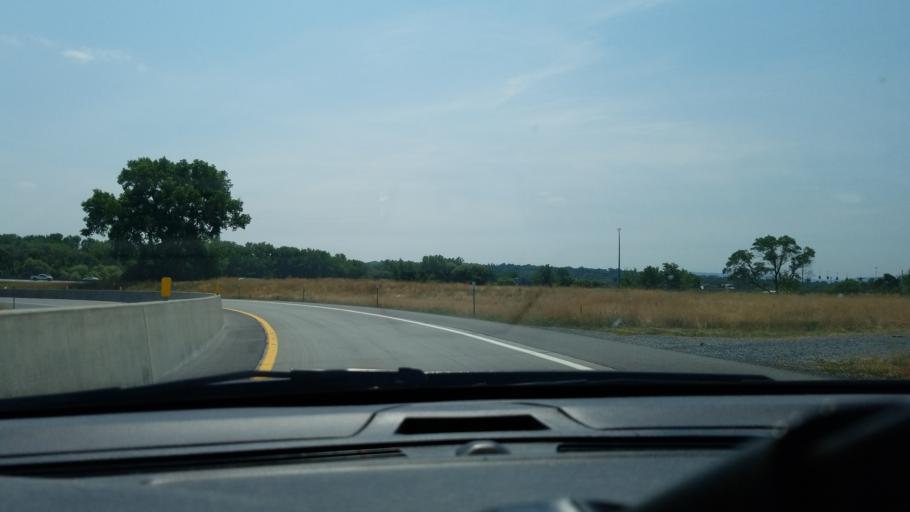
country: US
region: New York
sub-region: Onondaga County
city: Galeville
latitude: 43.0925
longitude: -76.1681
